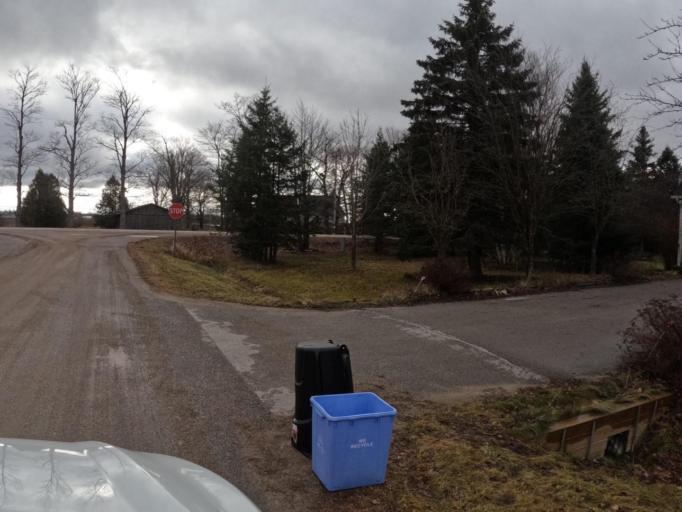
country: CA
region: Ontario
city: Shelburne
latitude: 43.9910
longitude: -80.3646
